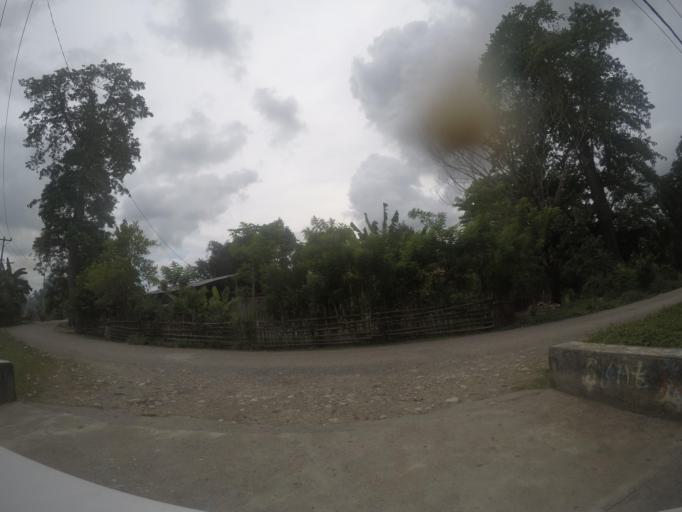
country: TL
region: Viqueque
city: Viqueque
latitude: -8.8780
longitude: 126.3686
